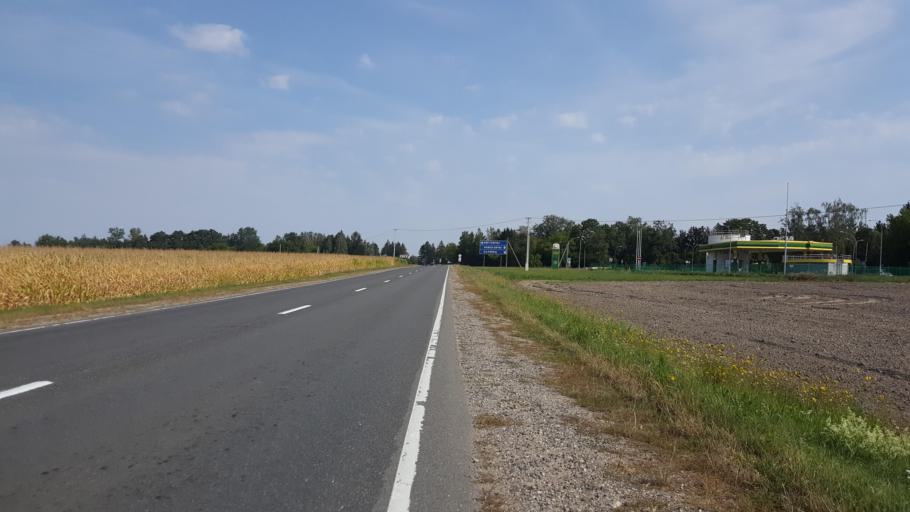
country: BY
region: Brest
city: Kamyanyets
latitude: 52.4093
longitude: 23.7868
